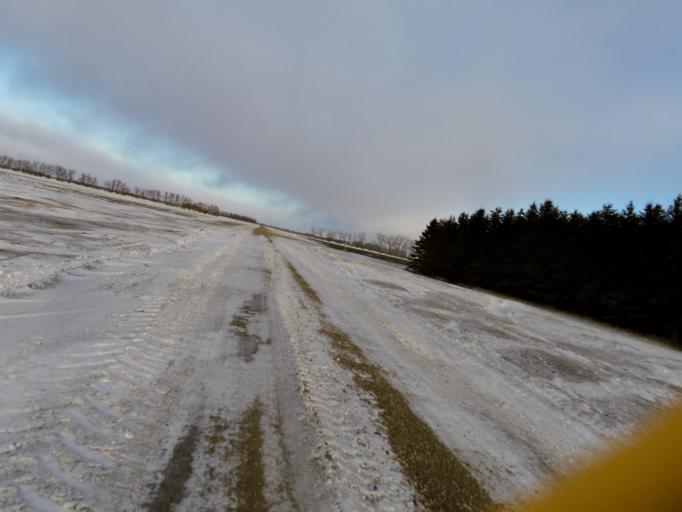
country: US
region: North Dakota
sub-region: Walsh County
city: Grafton
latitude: 48.3976
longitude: -97.2287
